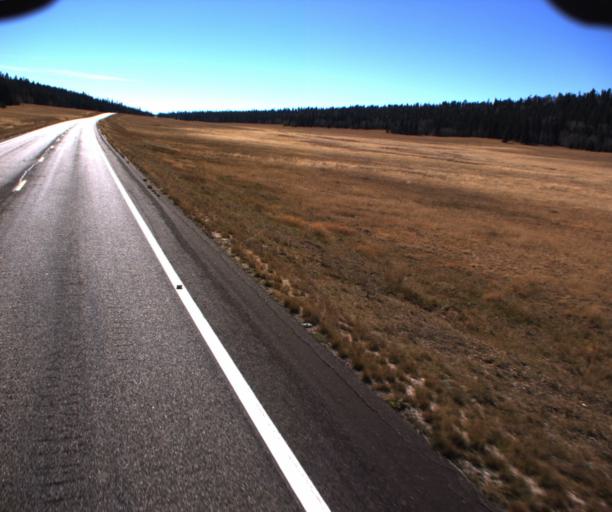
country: US
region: Arizona
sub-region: Coconino County
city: Grand Canyon
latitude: 36.3632
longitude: -112.1199
